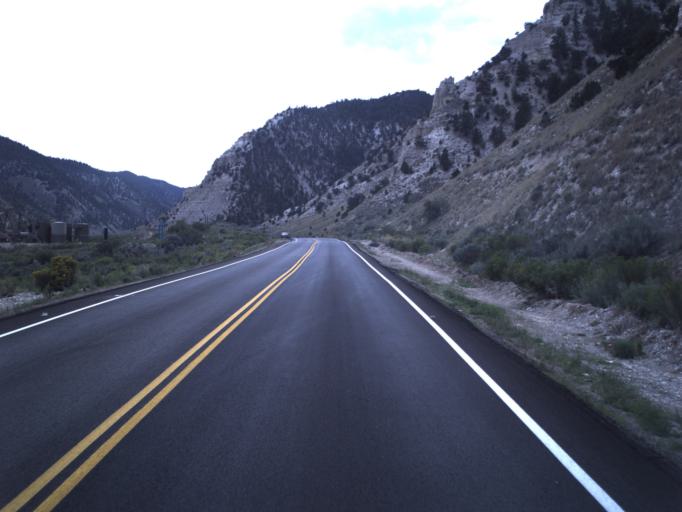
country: US
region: Utah
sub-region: Duchesne County
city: Duchesne
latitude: 40.0278
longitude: -110.5514
